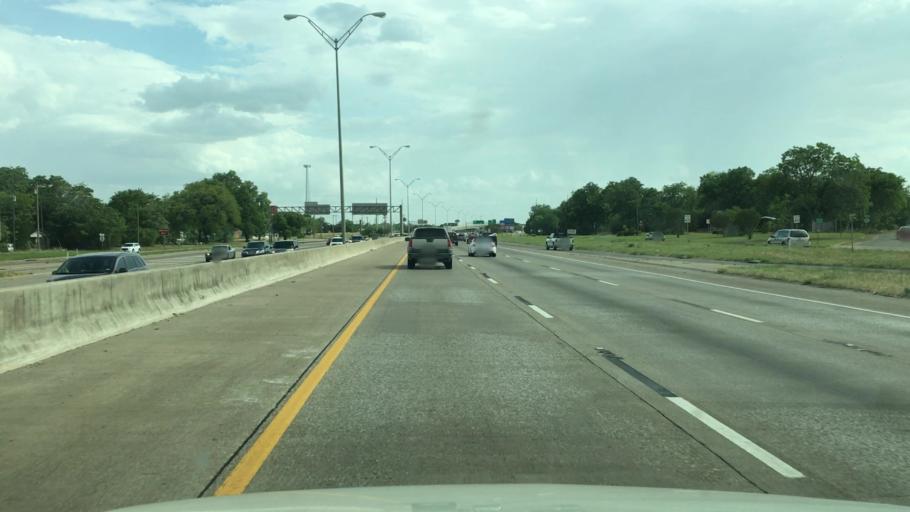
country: US
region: Texas
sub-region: McLennan County
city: Beverly
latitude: 31.5331
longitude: -97.1305
